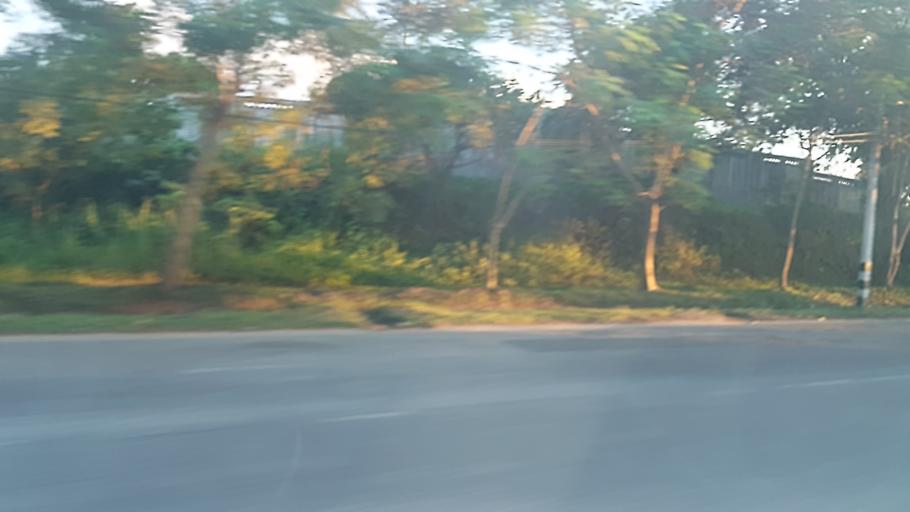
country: MM
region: Yangon
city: Yangon
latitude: 16.9041
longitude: 96.1272
